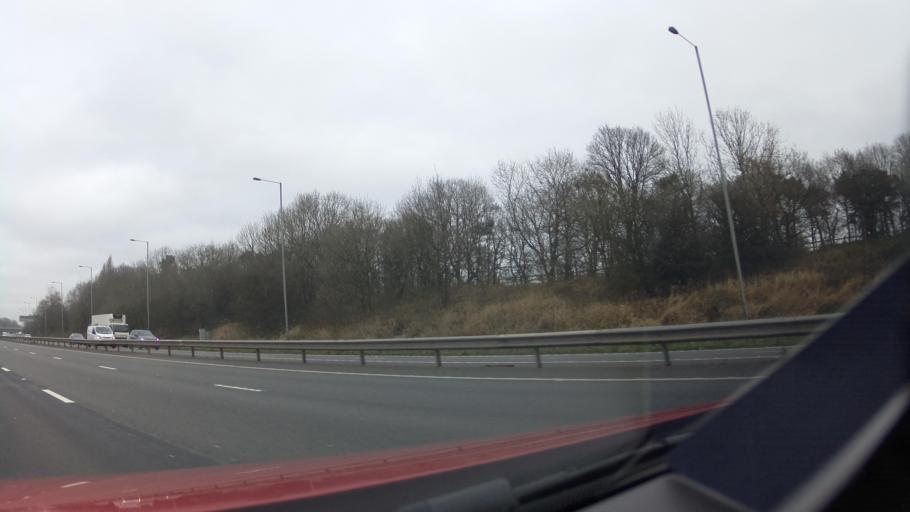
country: GB
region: England
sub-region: Lancashire
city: Euxton
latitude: 53.6600
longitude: -2.6908
